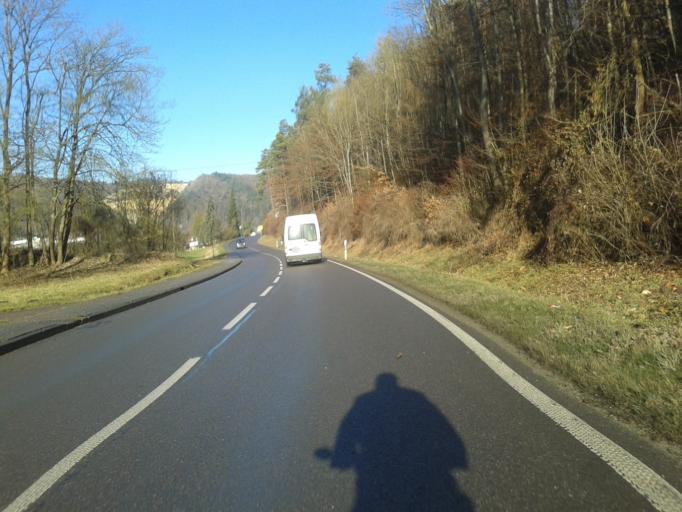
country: DE
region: Baden-Wuerttemberg
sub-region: Tuebingen Region
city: Erbach
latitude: 48.4077
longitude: 9.8718
